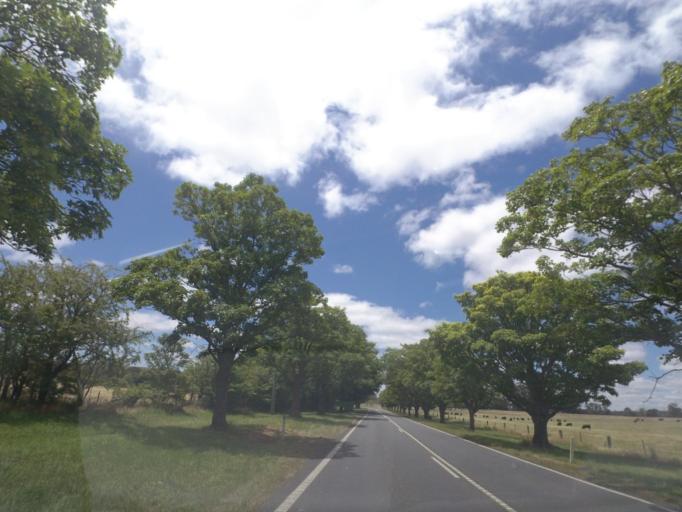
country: AU
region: Victoria
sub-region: Mount Alexander
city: Castlemaine
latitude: -37.3367
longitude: 144.1627
